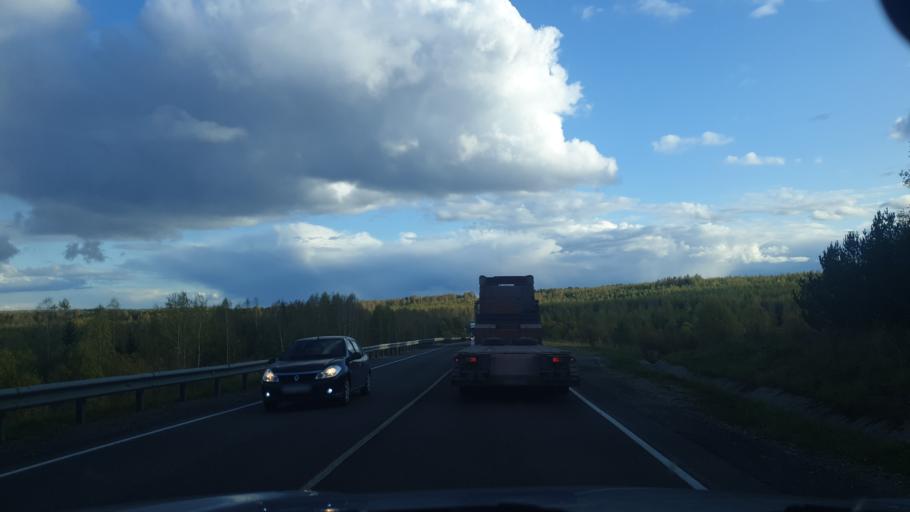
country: RU
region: Kirov
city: Murashi
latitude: 59.2305
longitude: 48.9882
